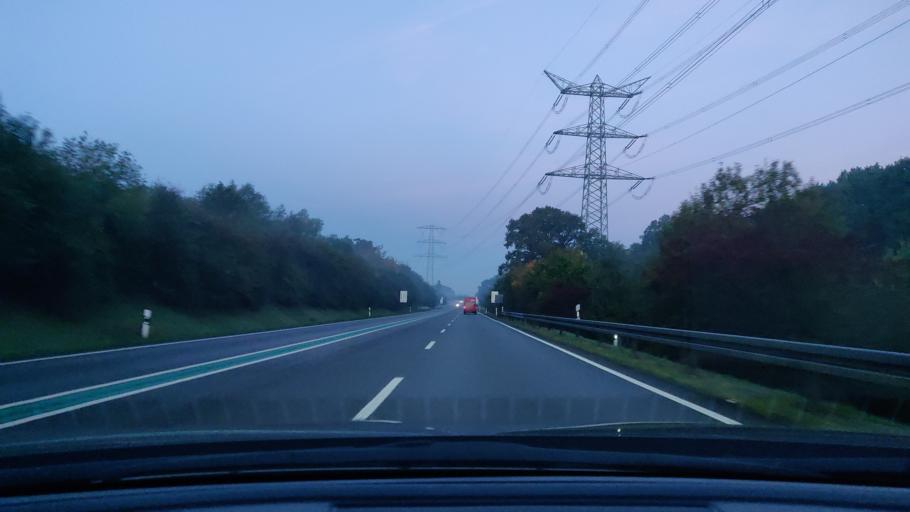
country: DE
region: North Rhine-Westphalia
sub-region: Regierungsbezirk Munster
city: Gronau
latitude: 52.1952
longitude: 7.0128
